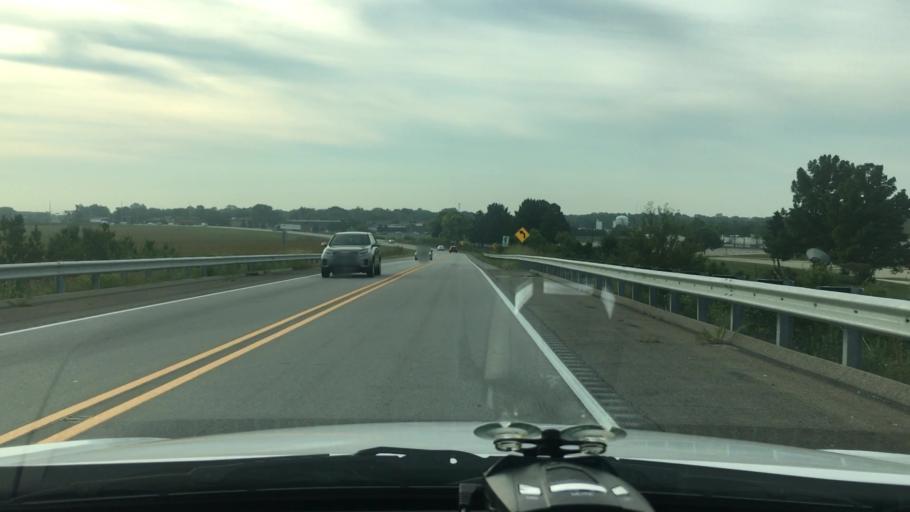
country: US
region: Illinois
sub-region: Champaign County
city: Champaign
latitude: 40.1417
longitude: -88.2856
